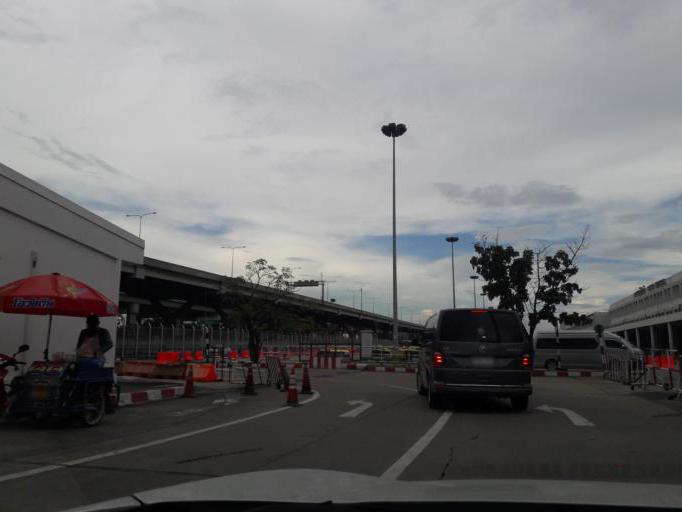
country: TH
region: Bangkok
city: Don Mueang
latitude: 13.9055
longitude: 100.5941
